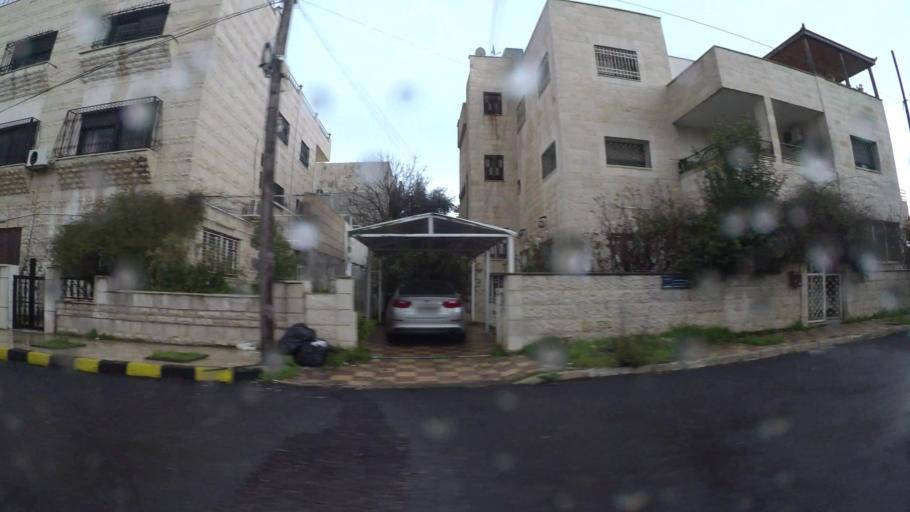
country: JO
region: Amman
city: Umm as Summaq
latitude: 31.8953
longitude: 35.8524
